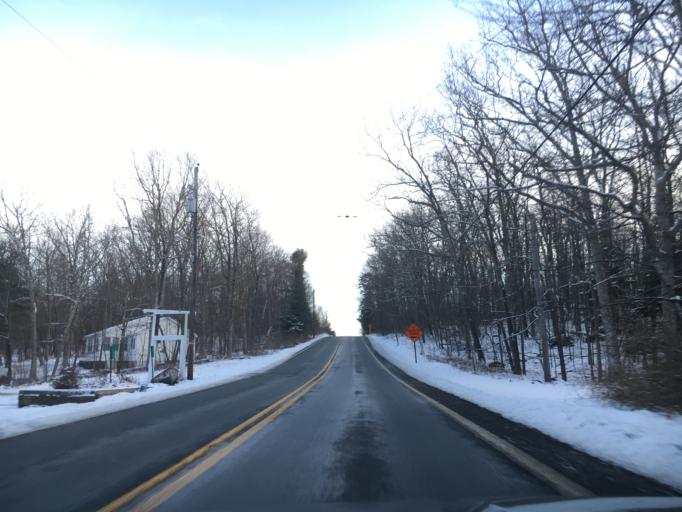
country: US
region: Pennsylvania
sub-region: Pike County
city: Hemlock Farms
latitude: 41.2832
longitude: -75.0922
